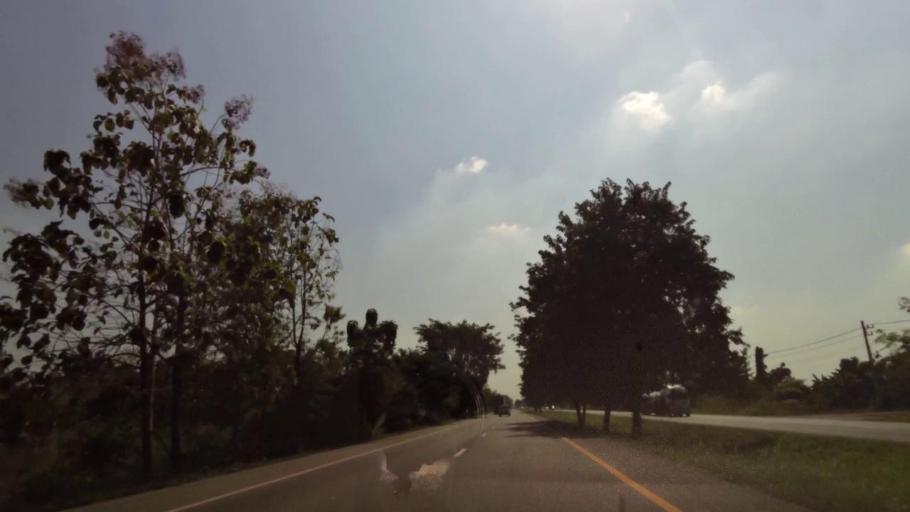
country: TH
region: Phichit
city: Bueng Na Rang
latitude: 16.2305
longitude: 100.1258
